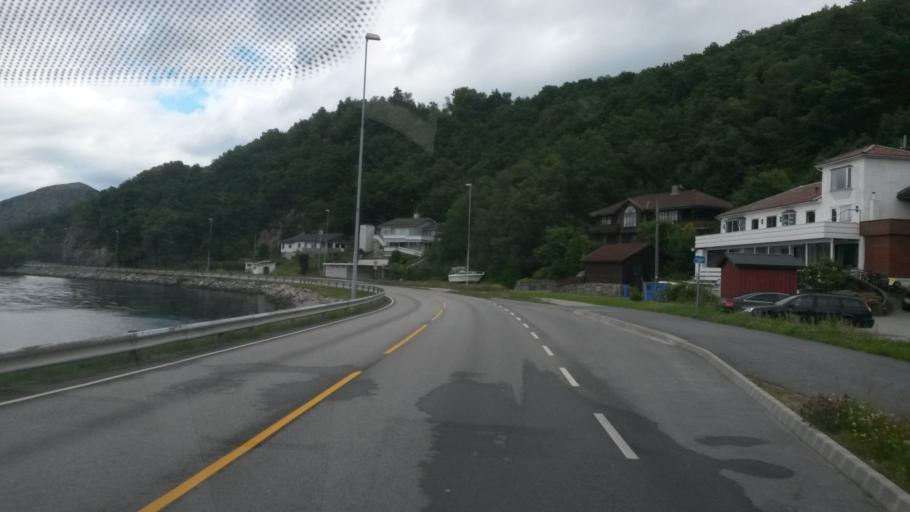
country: NO
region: Rogaland
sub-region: Sandnes
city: Sandnes
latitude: 58.8673
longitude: 5.7587
